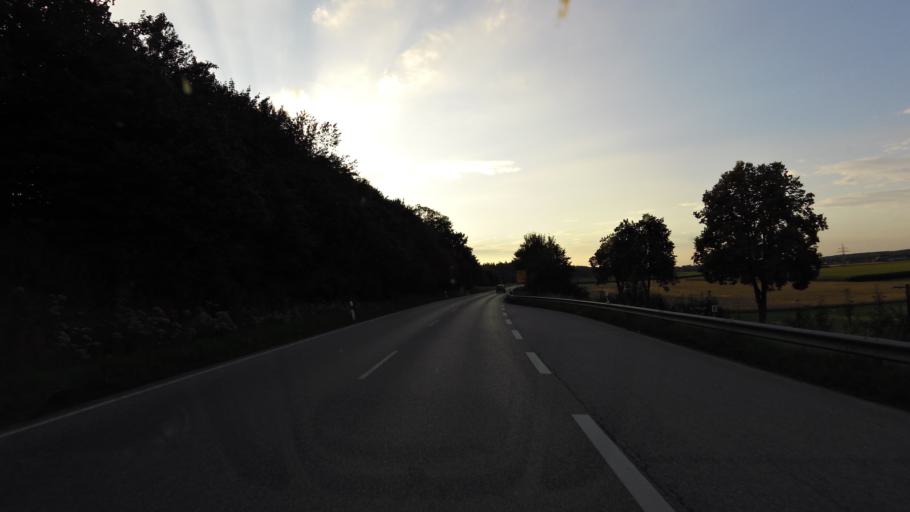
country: DE
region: Bavaria
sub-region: Upper Bavaria
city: Nussdorf
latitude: 47.9086
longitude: 12.6128
